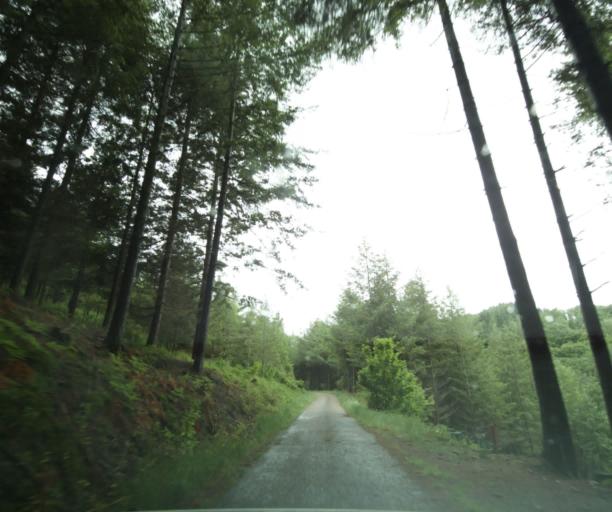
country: FR
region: Bourgogne
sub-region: Departement de Saone-et-Loire
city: Matour
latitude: 46.4474
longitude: 4.4678
